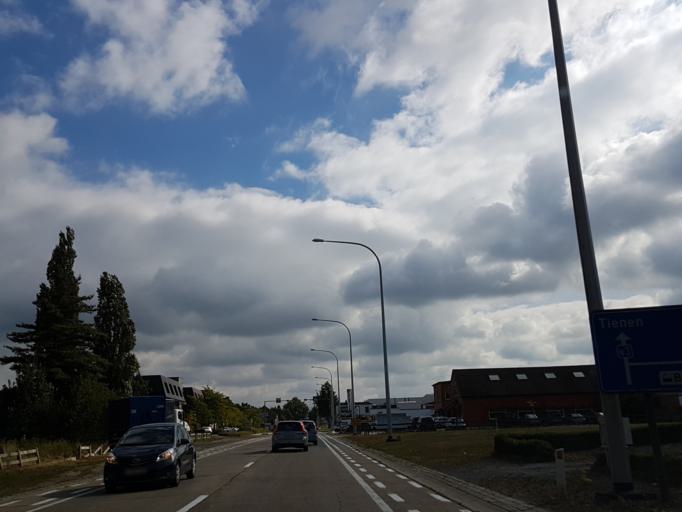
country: BE
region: Flanders
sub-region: Provincie Vlaams-Brabant
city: Boutersem
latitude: 50.8370
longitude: 4.8460
